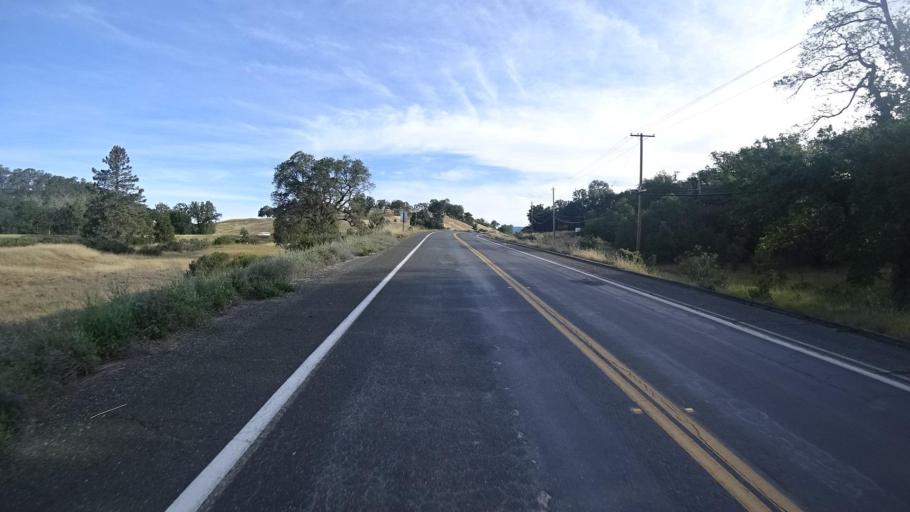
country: US
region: California
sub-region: Lake County
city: North Lakeport
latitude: 39.1121
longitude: -122.9068
